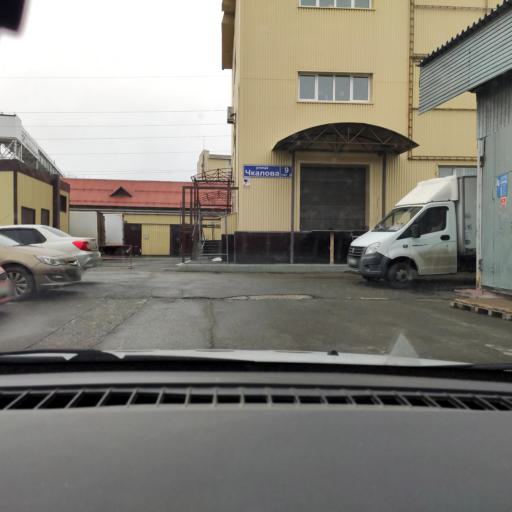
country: RU
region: Perm
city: Perm
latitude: 57.9848
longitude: 56.2646
